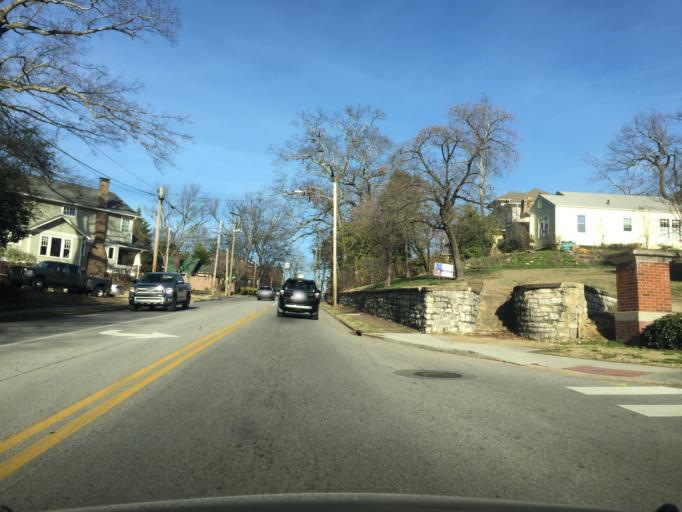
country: US
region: Tennessee
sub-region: Hamilton County
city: Chattanooga
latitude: 35.0634
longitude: -85.2982
